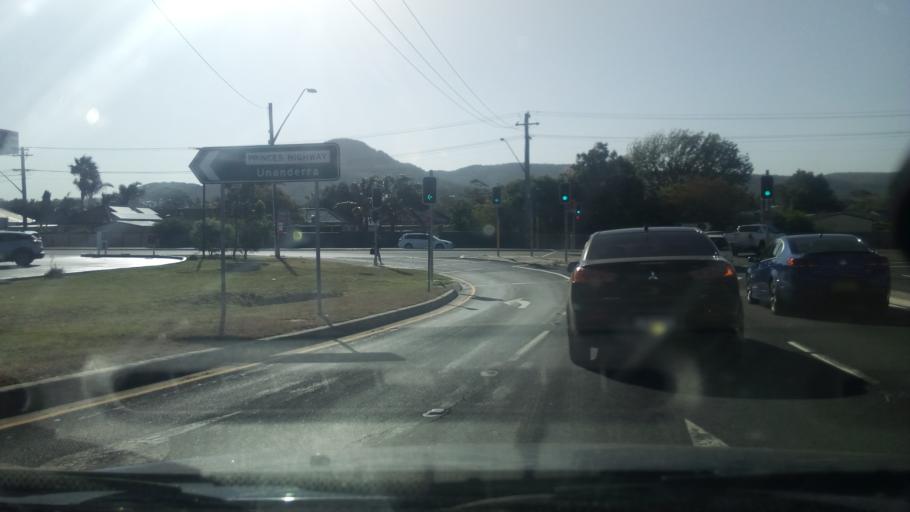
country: AU
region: New South Wales
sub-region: Wollongong
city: Cordeaux Heights
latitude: -34.4503
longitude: 150.8499
